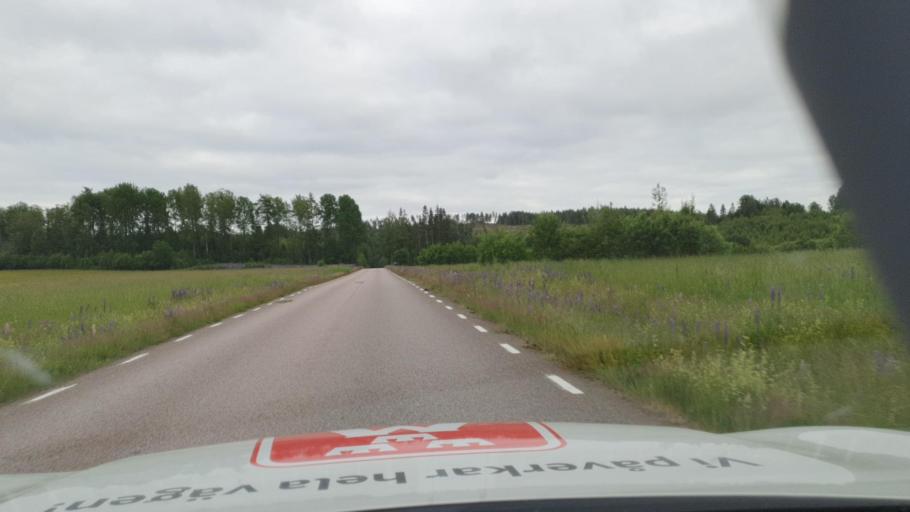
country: SE
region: Vaermland
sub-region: Kils Kommun
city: Kil
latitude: 59.6662
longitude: 13.2965
